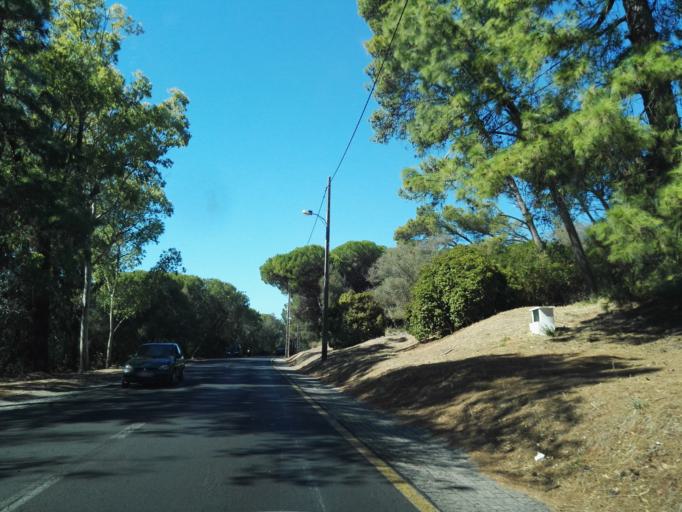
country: PT
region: Lisbon
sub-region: Odivelas
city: Pontinha
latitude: 38.7278
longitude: -9.1964
